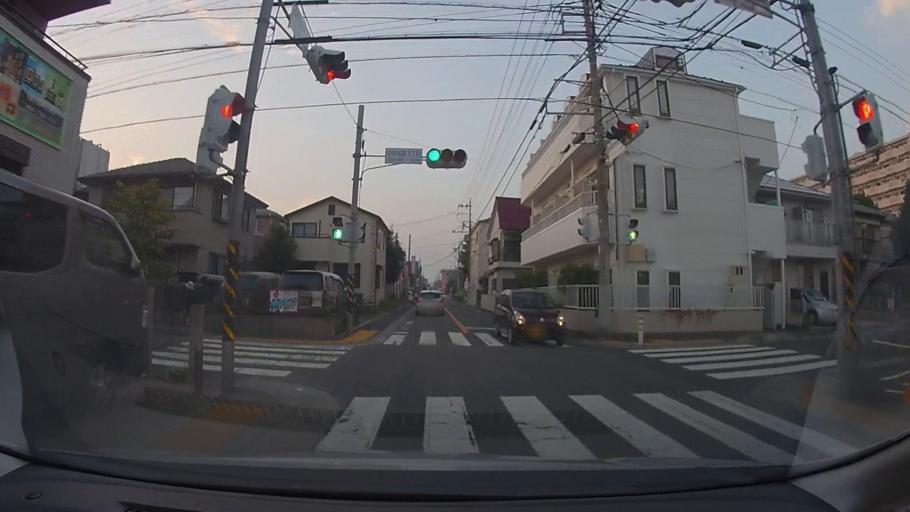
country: JP
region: Kanagawa
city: Minami-rinkan
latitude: 35.5021
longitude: 139.4430
